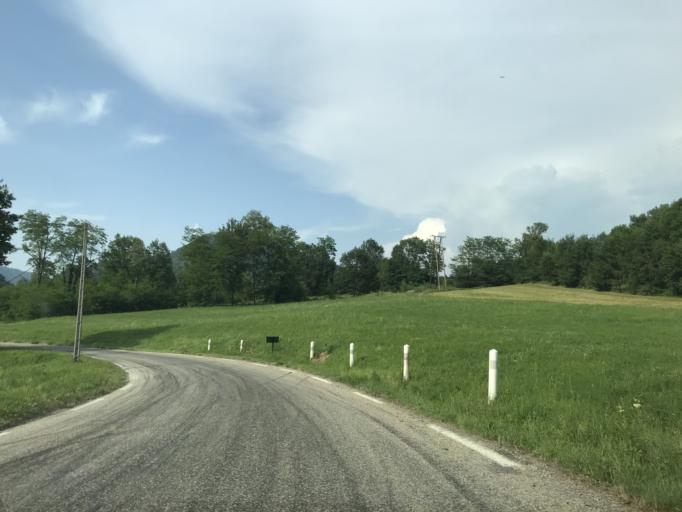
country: FR
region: Rhone-Alpes
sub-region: Departement de l'Isere
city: Allevard
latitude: 45.4237
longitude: 6.0929
